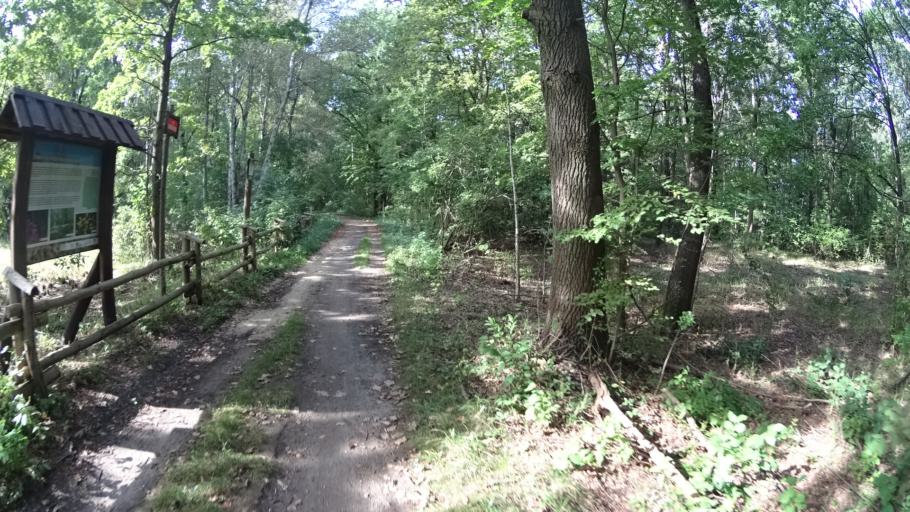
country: PL
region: Masovian Voivodeship
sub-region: Powiat warszawski zachodni
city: Babice
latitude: 52.2731
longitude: 20.8713
